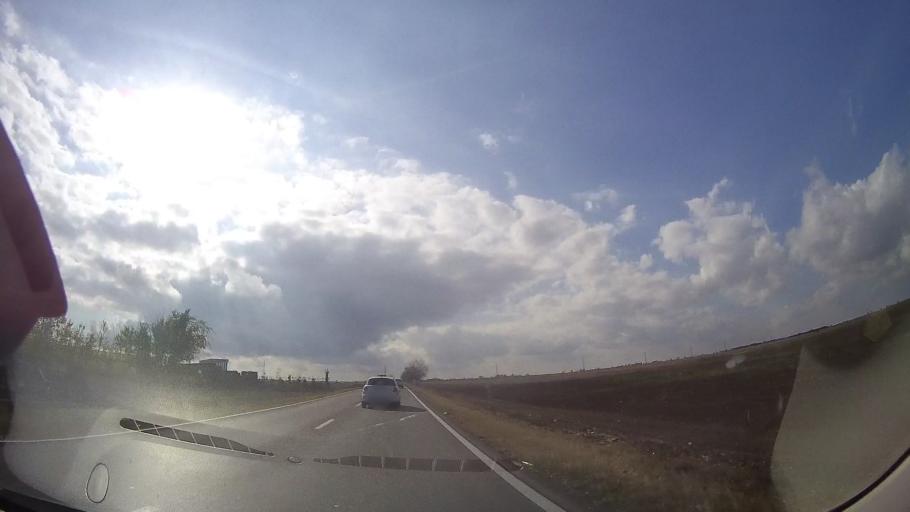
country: RO
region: Constanta
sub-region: Comuna Agigea
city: Agigea
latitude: 44.0790
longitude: 28.6025
